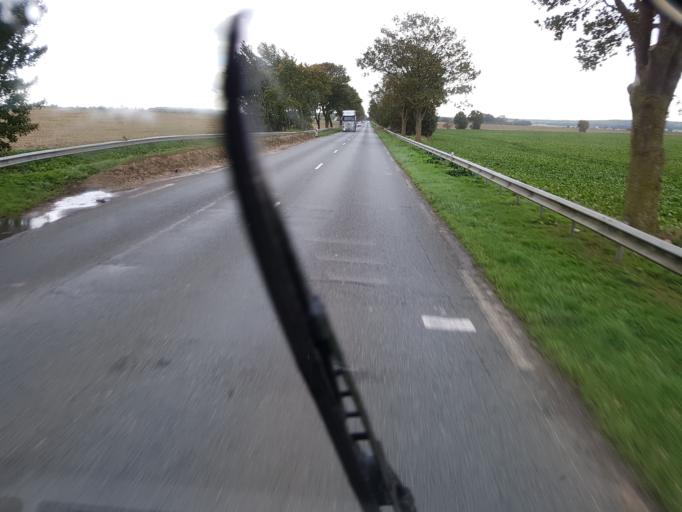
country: FR
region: Picardie
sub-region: Departement de l'Oise
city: Le Plessis-Belleville
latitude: 49.0762
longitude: 2.7650
